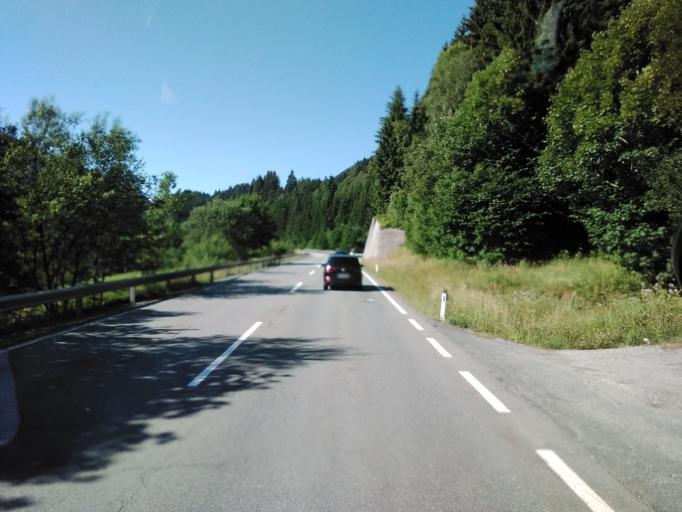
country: AT
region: Tyrol
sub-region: Politischer Bezirk Kitzbuhel
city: Jochberg
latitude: 47.3643
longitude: 12.4148
